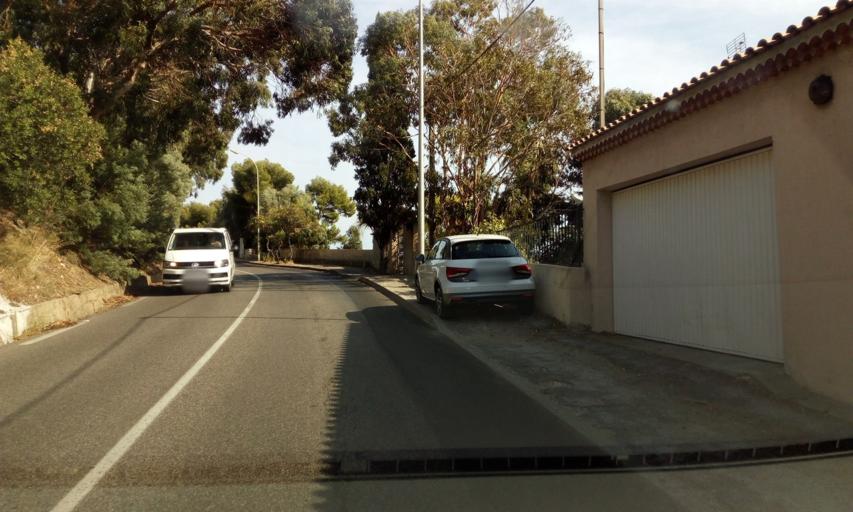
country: FR
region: Provence-Alpes-Cote d'Azur
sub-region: Departement du Var
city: Le Lavandou
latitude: 43.1448
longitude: 6.3884
